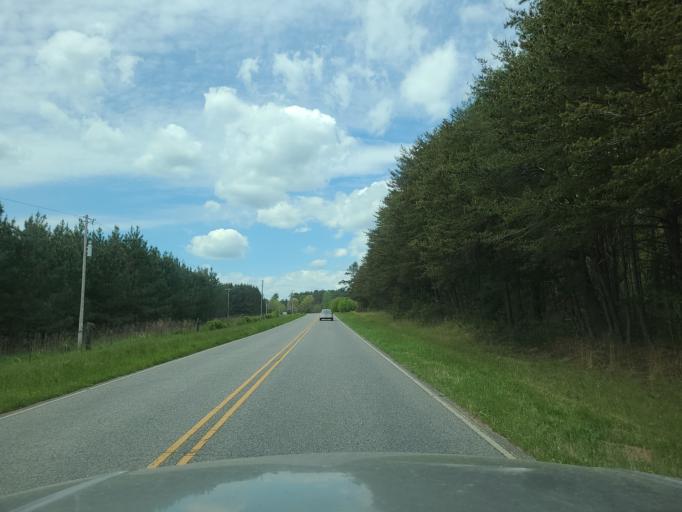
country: US
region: North Carolina
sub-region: Cleveland County
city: Boiling Springs
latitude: 35.4505
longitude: -81.6644
